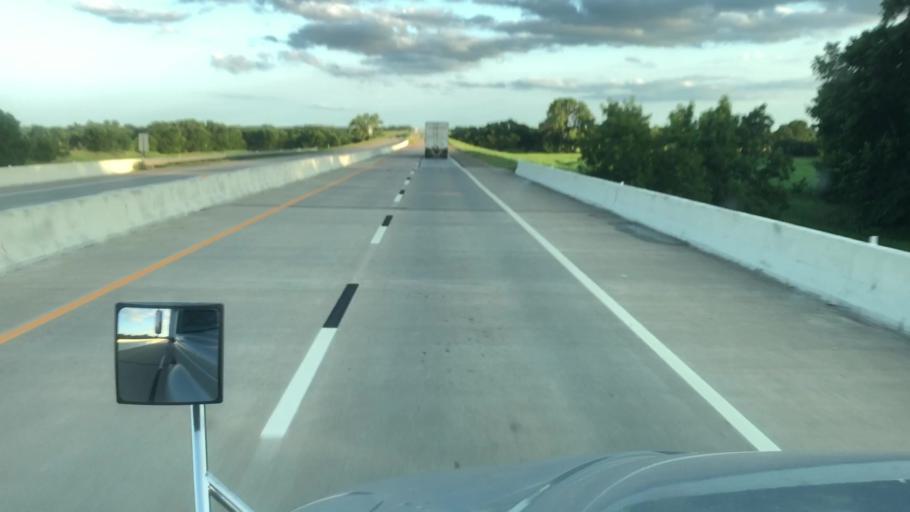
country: US
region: Oklahoma
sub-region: Pawnee County
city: Pawnee
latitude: 36.3079
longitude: -96.9908
